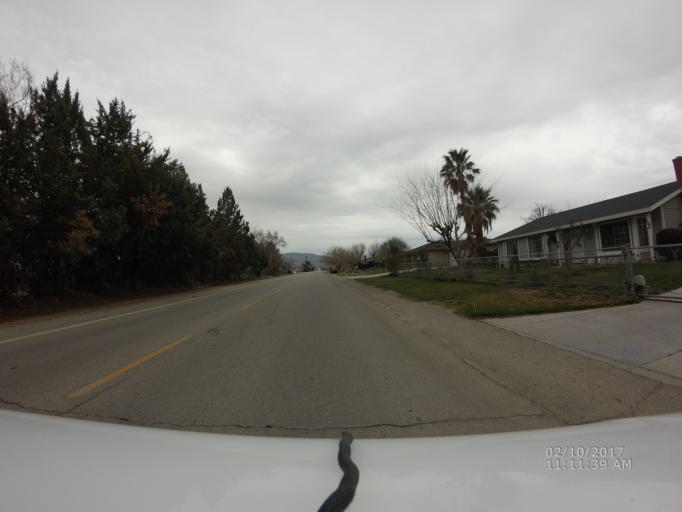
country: US
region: California
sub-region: Los Angeles County
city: Littlerock
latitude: 34.5514
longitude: -117.9582
